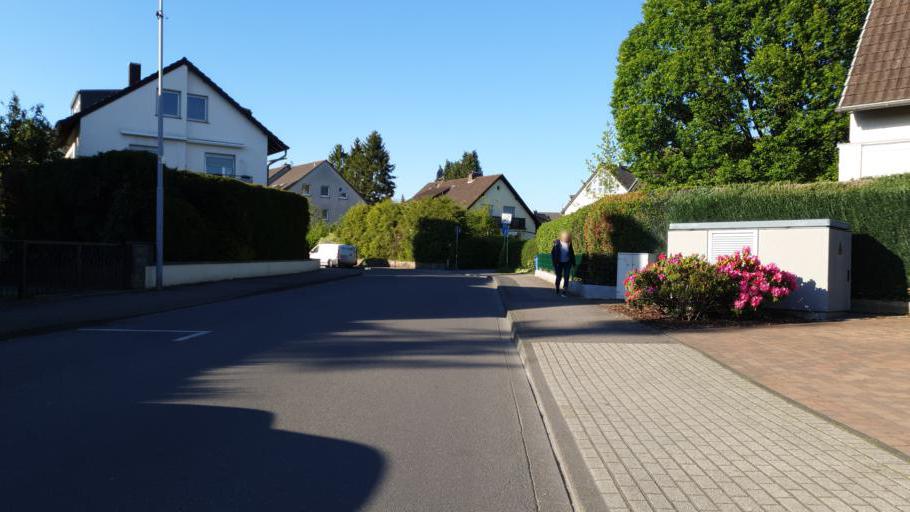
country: DE
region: North Rhine-Westphalia
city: Opladen
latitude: 51.0600
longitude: 7.0524
